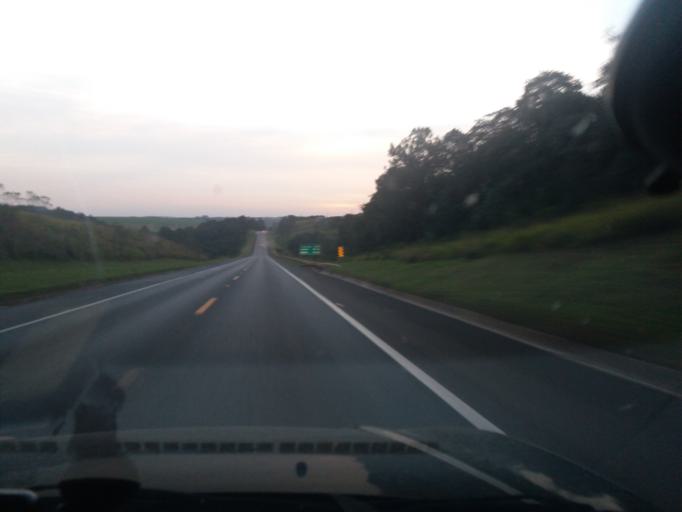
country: BR
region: Sao Paulo
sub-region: Buri
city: Buri
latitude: -23.9360
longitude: -48.6259
